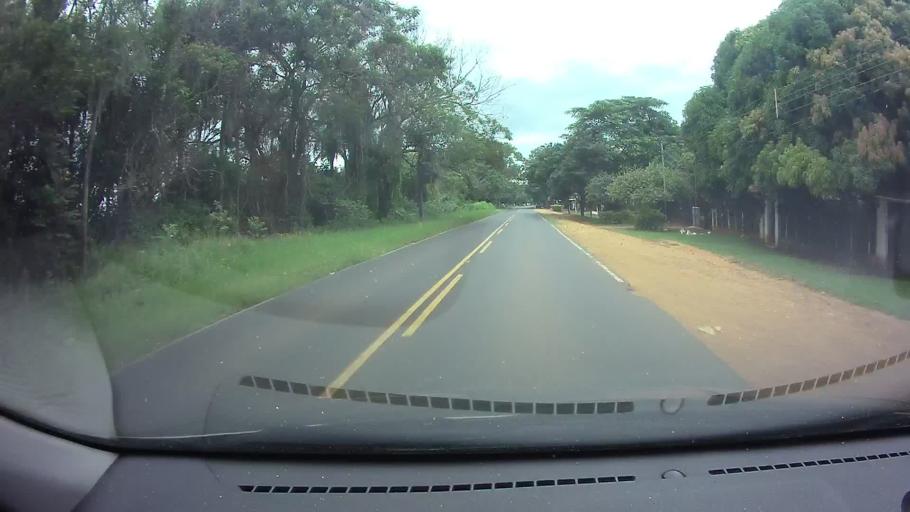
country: PY
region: Central
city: Guarambare
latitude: -25.5289
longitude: -57.4978
